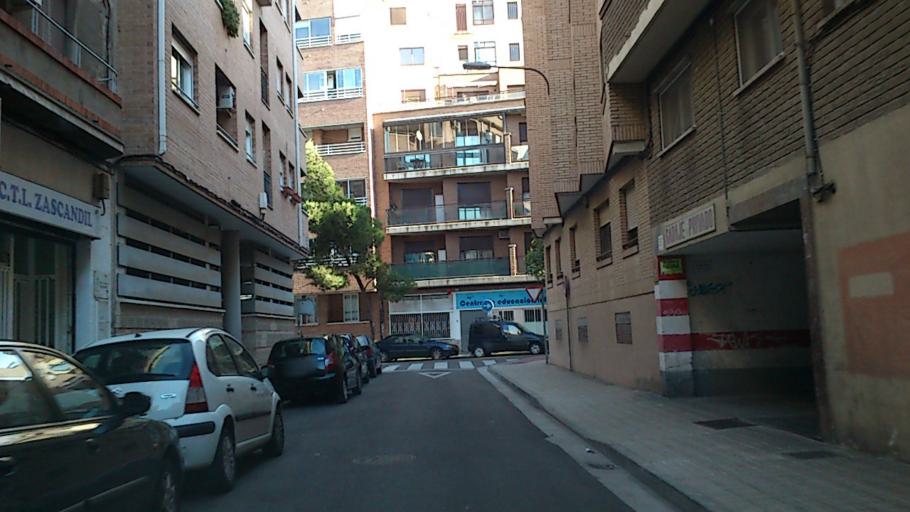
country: ES
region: Aragon
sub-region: Provincia de Zaragoza
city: Zaragoza
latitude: 41.6590
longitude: -0.8696
